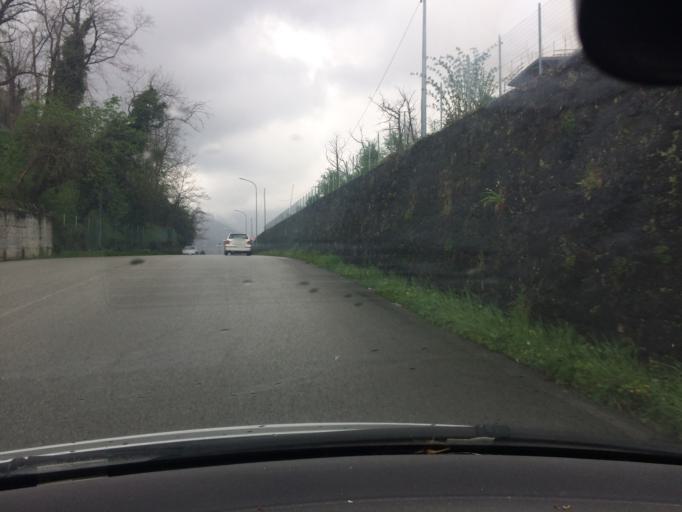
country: IT
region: Tuscany
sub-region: Provincia di Massa-Carrara
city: Massa
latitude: 44.0656
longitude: 10.1113
